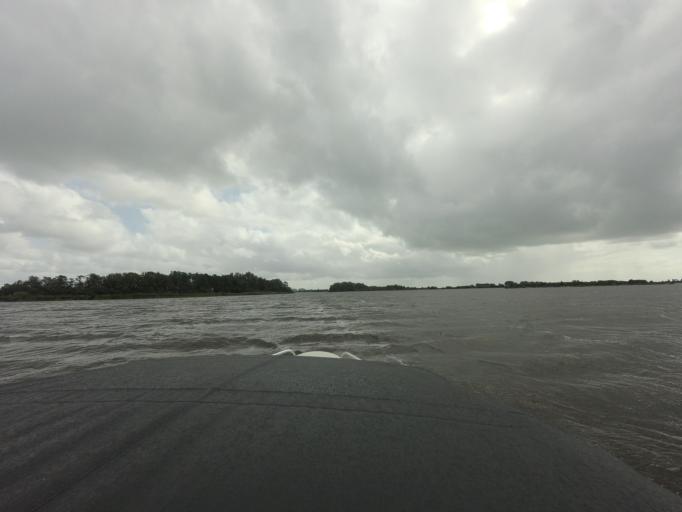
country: NL
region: Friesland
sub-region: Gemeente Boarnsterhim
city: Warten
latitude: 53.1134
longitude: 5.9246
